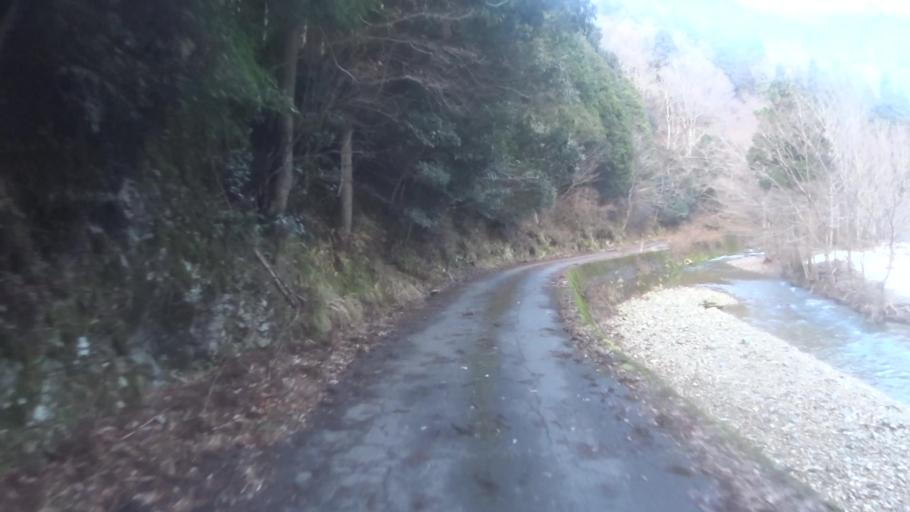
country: JP
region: Kyoto
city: Maizuru
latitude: 35.3979
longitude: 135.4874
